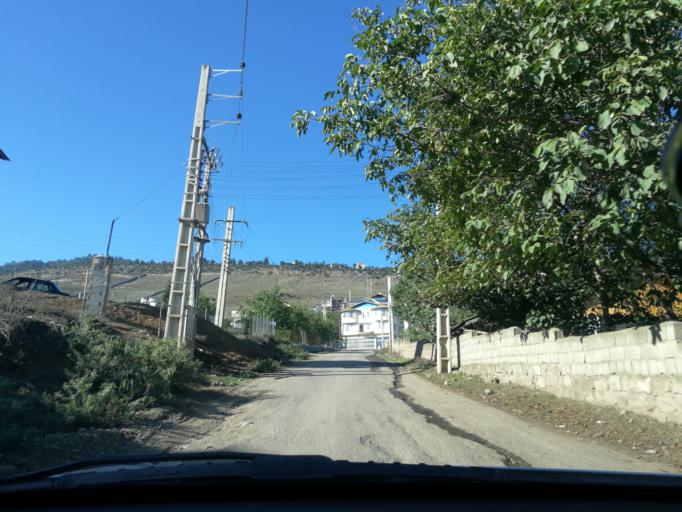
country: IR
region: Mazandaran
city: `Abbasabad
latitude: 36.5555
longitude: 51.1933
